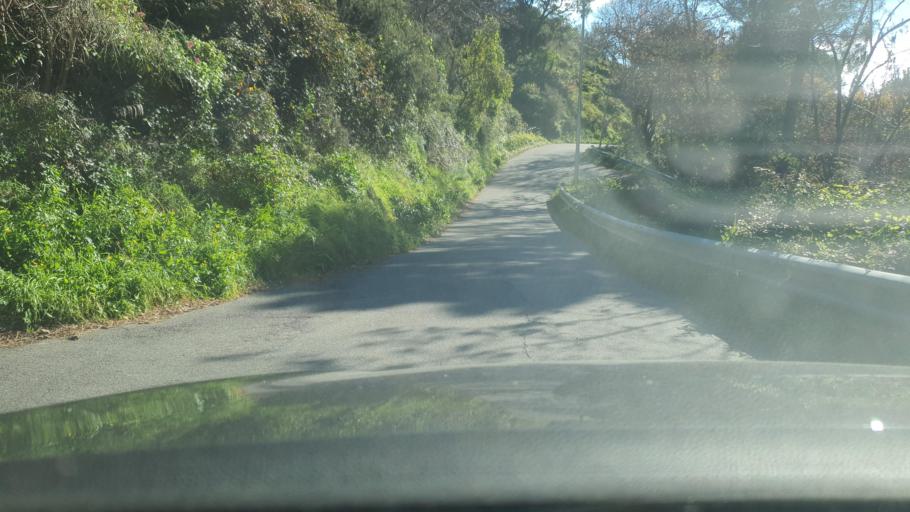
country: IT
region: Calabria
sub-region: Provincia di Catanzaro
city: Sant'Elia
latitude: 38.9599
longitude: 16.5784
